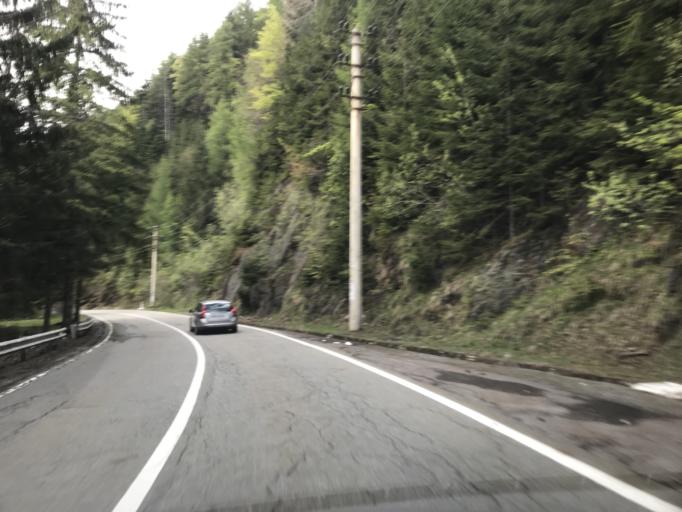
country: RO
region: Sibiu
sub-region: Comuna Cartisoara
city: Cartisoara
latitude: 45.6551
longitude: 24.6027
